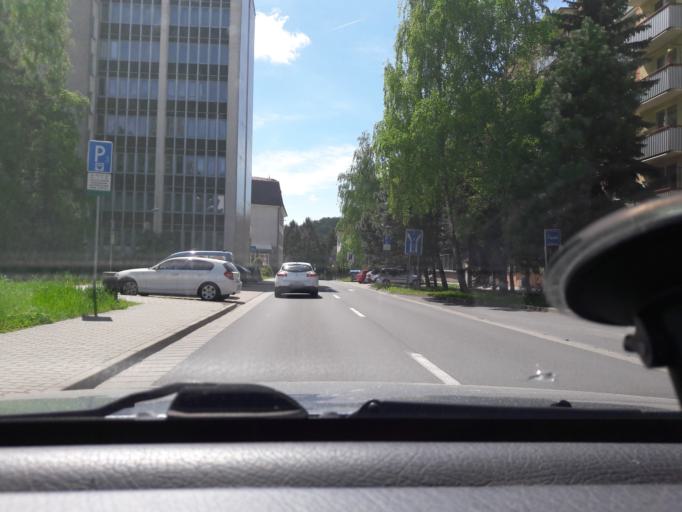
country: SK
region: Banskobystricky
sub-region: Okres Banska Bystrica
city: Zvolen
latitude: 48.5741
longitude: 19.1237
